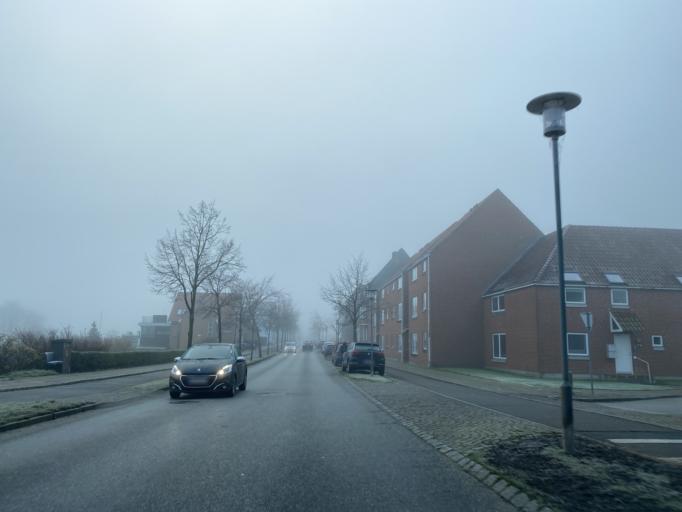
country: DK
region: Central Jutland
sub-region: Skanderborg Kommune
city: Skanderborg
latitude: 56.0426
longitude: 9.9296
